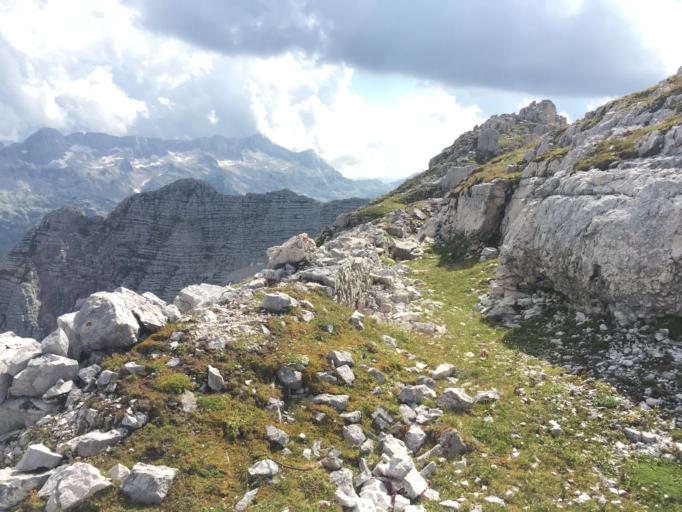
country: IT
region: Friuli Venezia Giulia
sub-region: Provincia di Udine
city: Malborghetto
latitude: 46.4229
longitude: 13.4882
